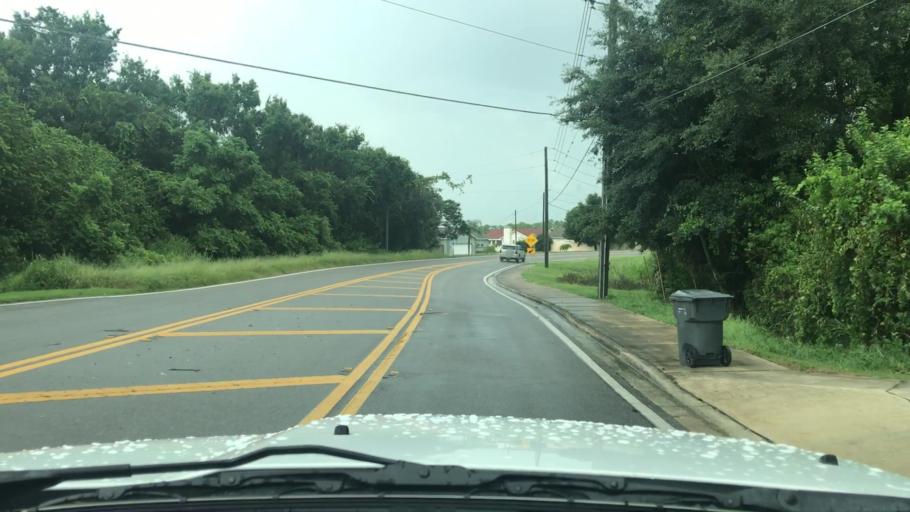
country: US
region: Florida
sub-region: Polk County
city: Cypress Gardens
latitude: 28.0071
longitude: -81.6861
